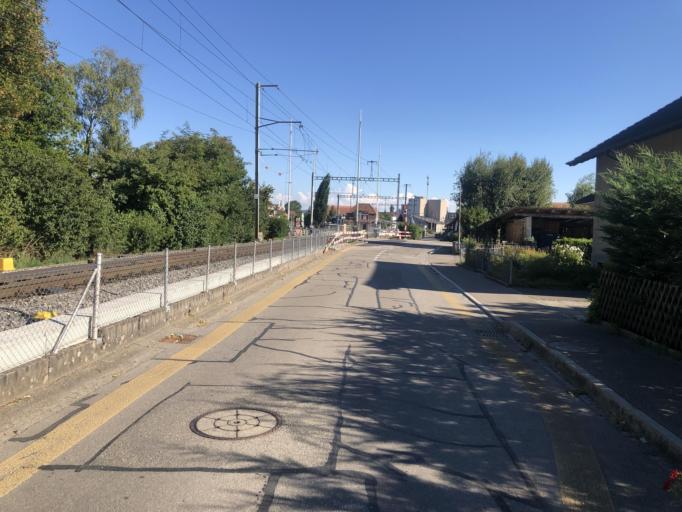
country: CH
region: Bern
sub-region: Bern-Mittelland District
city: Fraubrunnen
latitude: 47.0884
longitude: 7.5214
